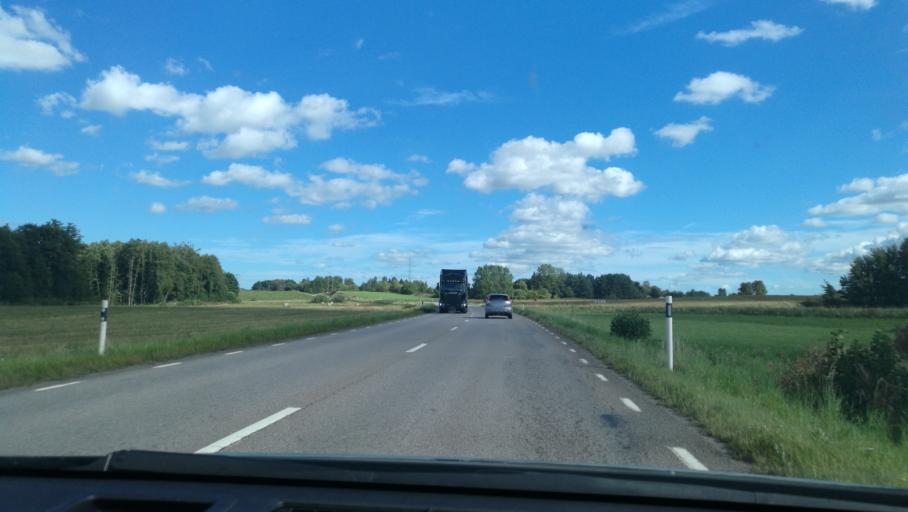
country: SE
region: Vaestra Goetaland
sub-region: Gotene Kommun
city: Kallby
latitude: 58.4919
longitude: 13.2903
